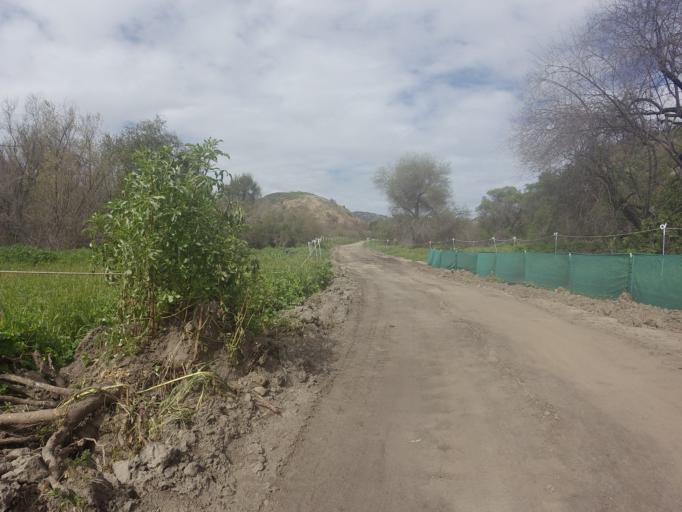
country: US
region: California
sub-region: Orange County
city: Aliso Viejo
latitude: 33.5526
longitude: -117.7413
